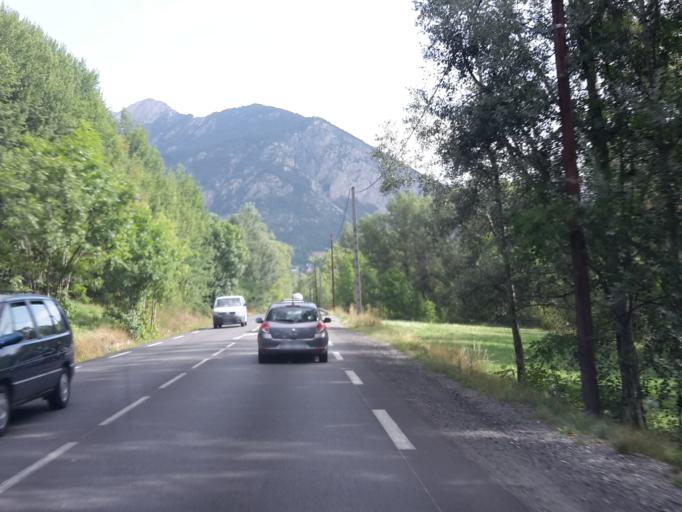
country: FR
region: Provence-Alpes-Cote d'Azur
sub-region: Departement des Hautes-Alpes
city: Villar-Saint-Pancrace
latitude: 44.8849
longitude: 6.6235
